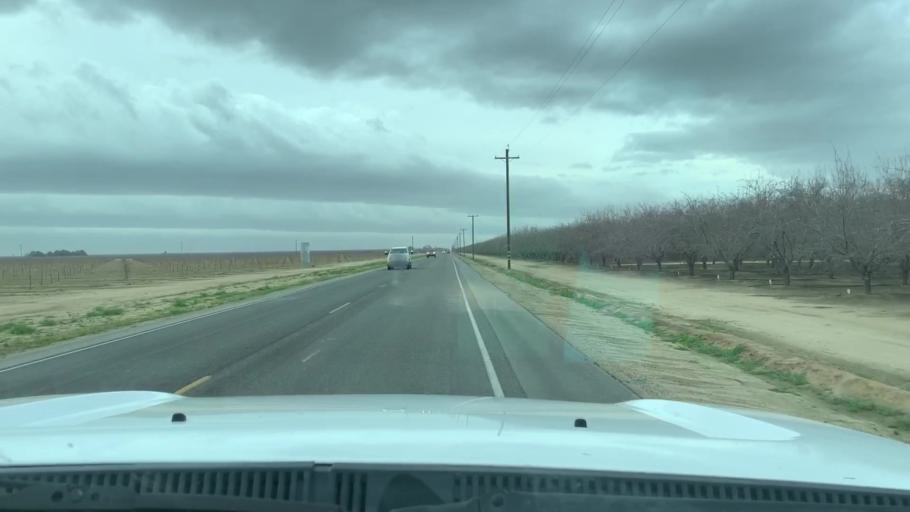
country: US
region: California
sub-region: Kern County
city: Wasco
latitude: 35.5581
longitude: -119.2989
